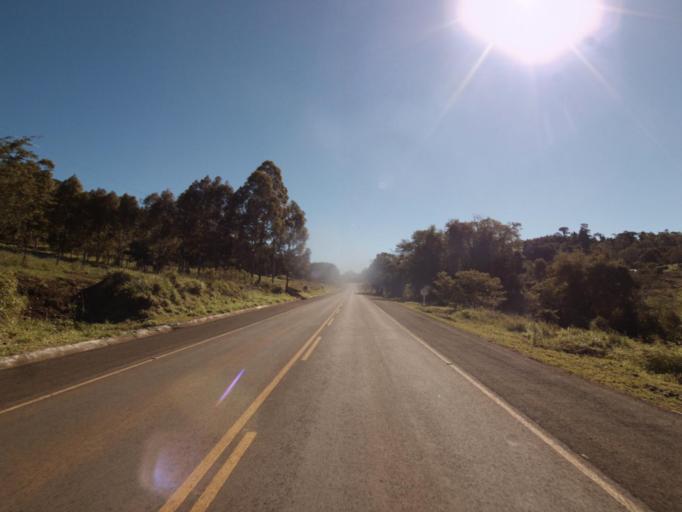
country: AR
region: Misiones
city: Bernardo de Irigoyen
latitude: -26.6840
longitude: -53.5502
